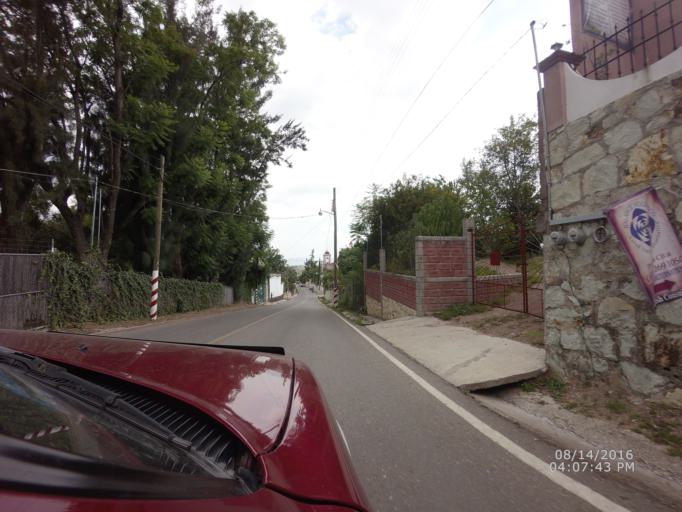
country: MX
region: Oaxaca
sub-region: San Juan Bautista Guelache
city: Fraccionamiento San Miguel
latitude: 17.1909
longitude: -96.7642
